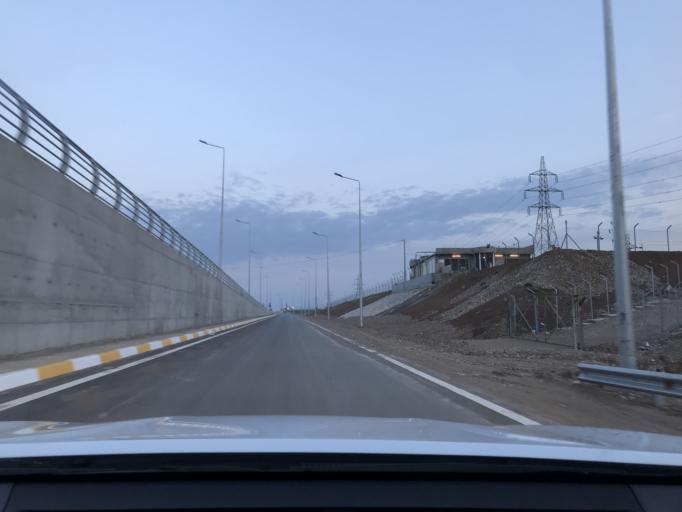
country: IQ
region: Arbil
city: Erbil
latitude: 36.3156
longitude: 43.9099
